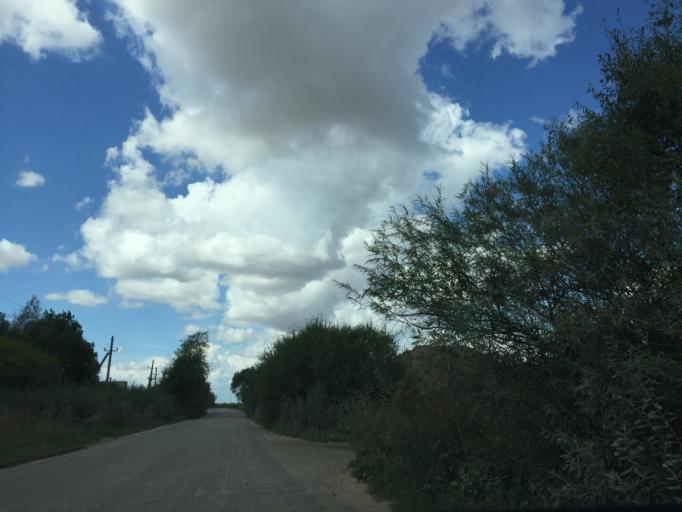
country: LV
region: Rundales
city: Pilsrundale
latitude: 56.3002
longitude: 23.9919
